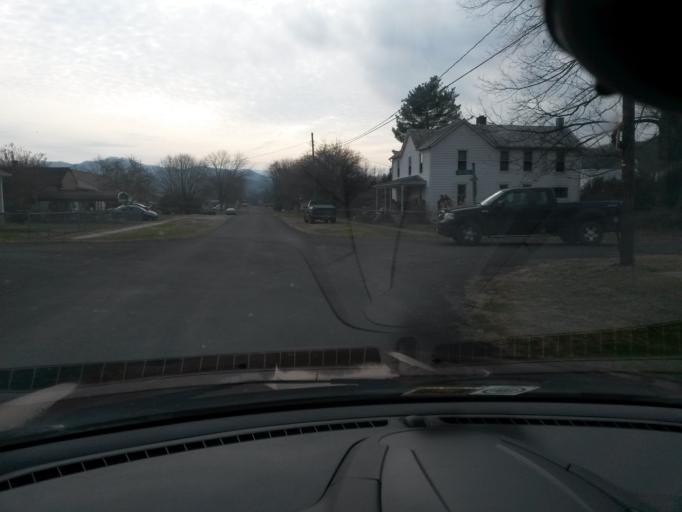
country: US
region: Virginia
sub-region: Alleghany County
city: Clifton Forge
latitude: 37.7968
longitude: -79.7889
